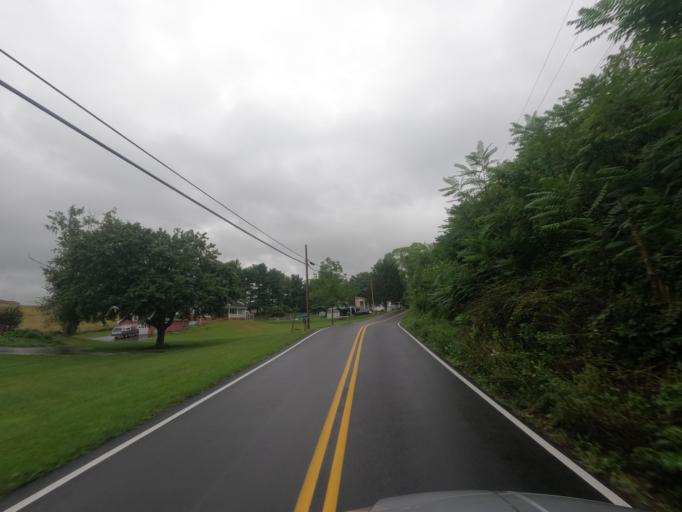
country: US
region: Maryland
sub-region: Washington County
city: Wilson-Conococheague
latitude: 39.6415
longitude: -77.9319
